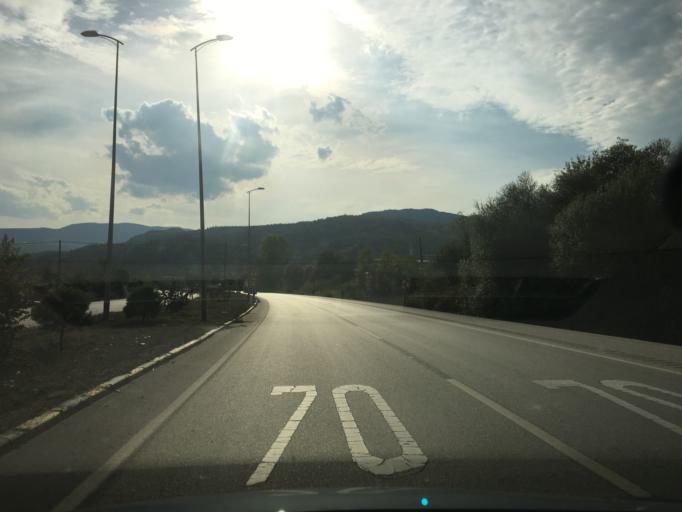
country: TR
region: Karabuk
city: Karabuk
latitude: 41.1211
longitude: 32.6778
